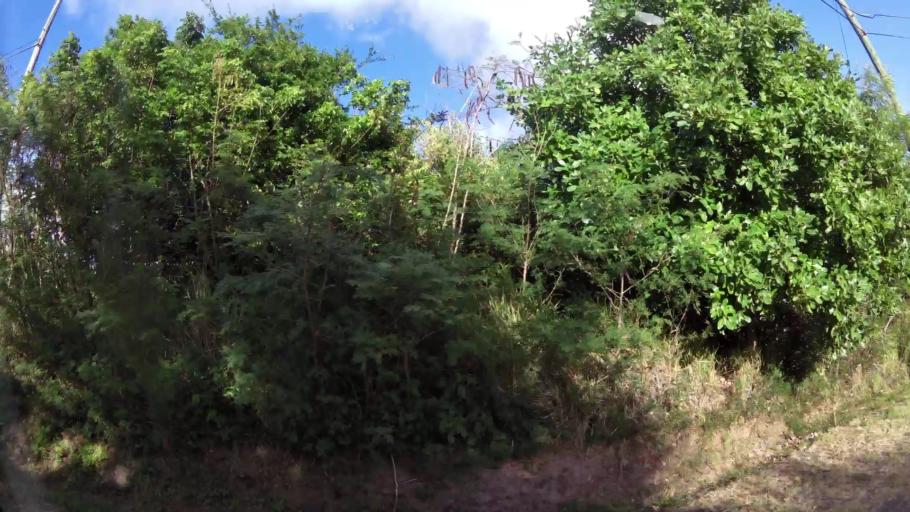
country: LC
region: Gros-Islet
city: Gros Islet
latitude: 14.1007
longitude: -60.9367
